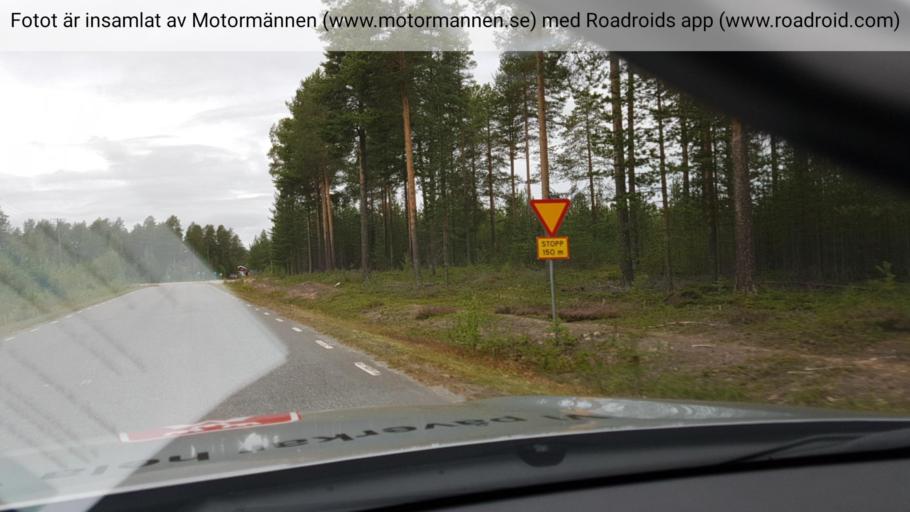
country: SE
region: Norrbotten
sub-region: Bodens Kommun
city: Boden
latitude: 65.8153
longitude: 21.5906
